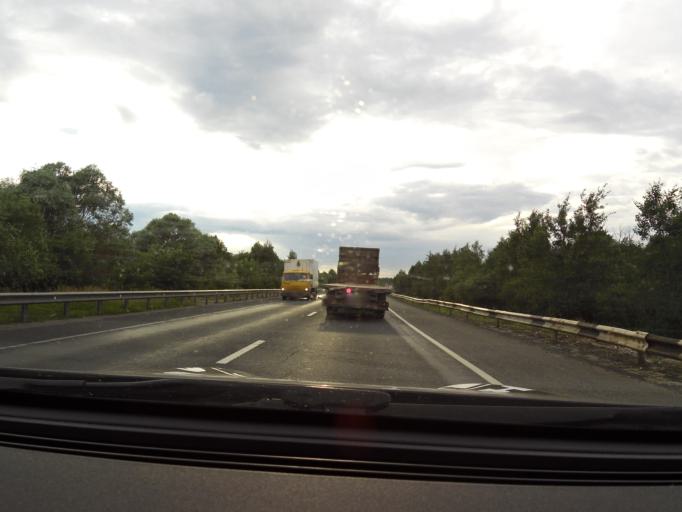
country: RU
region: Vladimir
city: Raduzhnyy
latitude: 56.0588
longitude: 40.3836
